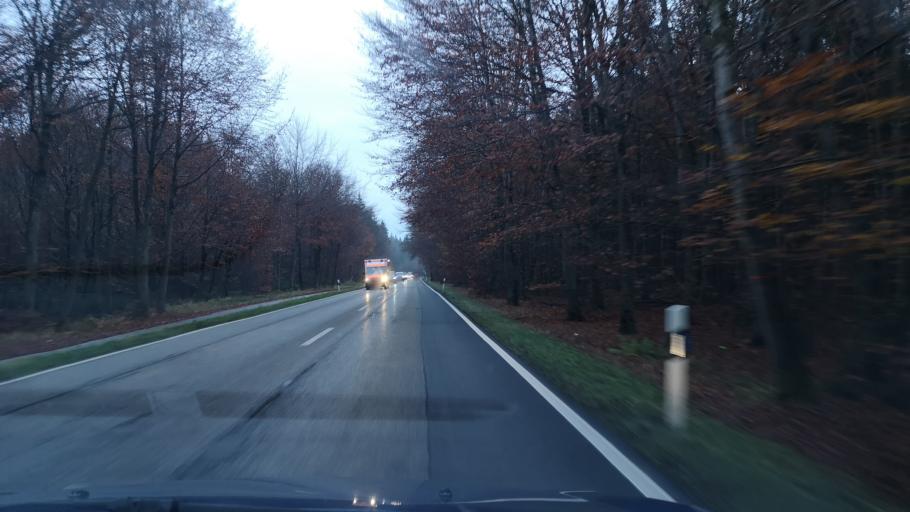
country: DE
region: Bavaria
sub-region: Upper Bavaria
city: Ebersberg
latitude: 48.1094
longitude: 11.9545
